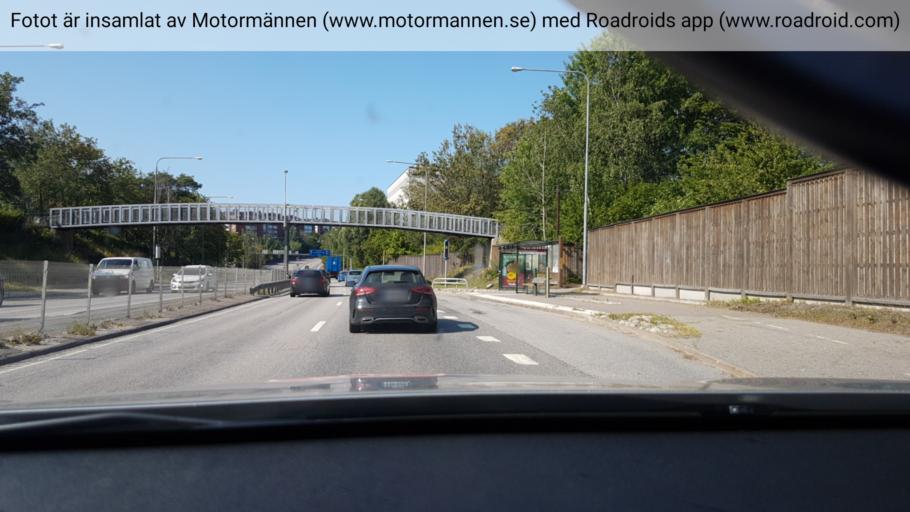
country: SE
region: Stockholm
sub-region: Huddinge Kommun
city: Huddinge
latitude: 59.2452
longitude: 17.9975
